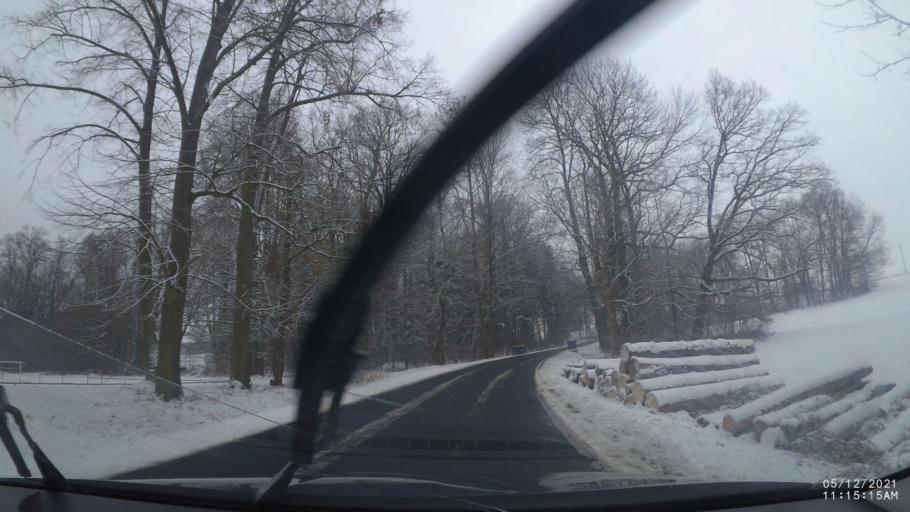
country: CZ
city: Solnice
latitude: 50.1859
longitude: 16.2162
